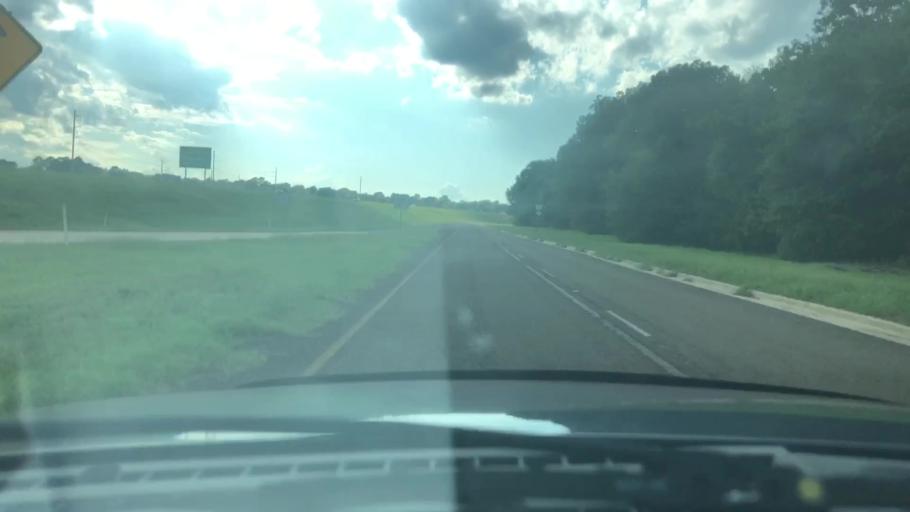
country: US
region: Texas
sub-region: Bowie County
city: Wake Village
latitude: 33.3865
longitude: -94.0856
